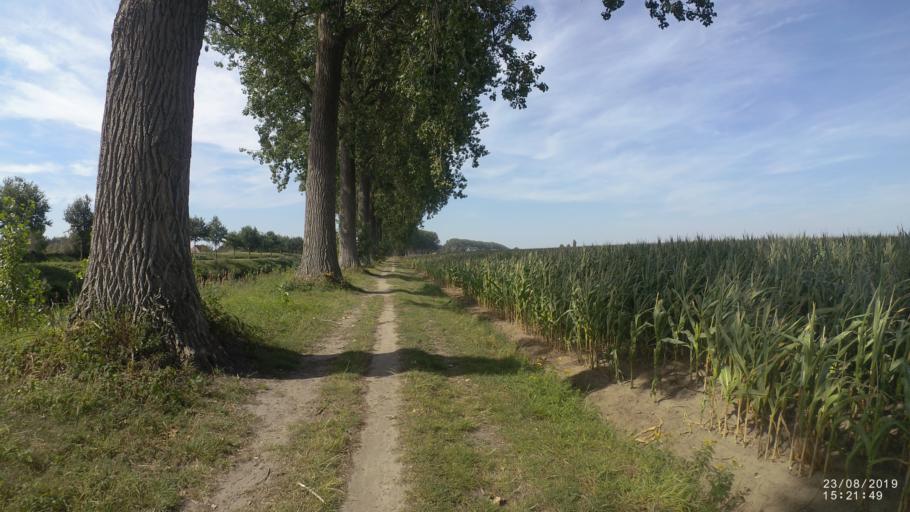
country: BE
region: Flanders
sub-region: Provincie Oost-Vlaanderen
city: Zomergem
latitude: 51.1244
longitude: 3.5687
